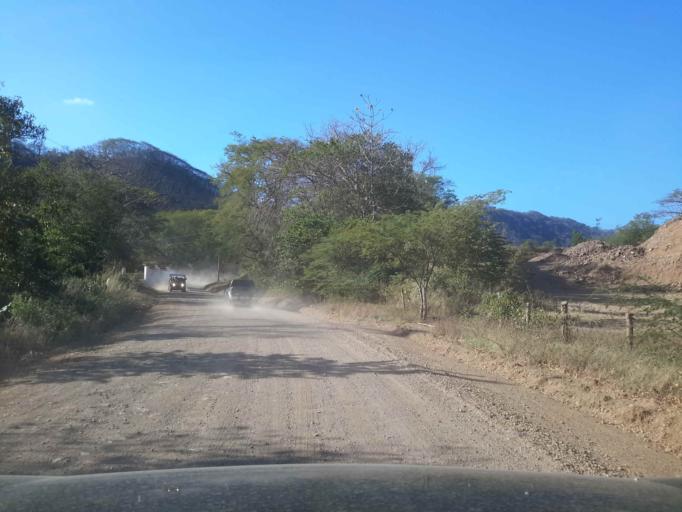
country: NI
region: Rivas
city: San Juan del Sur
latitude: 11.1896
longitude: -85.8099
